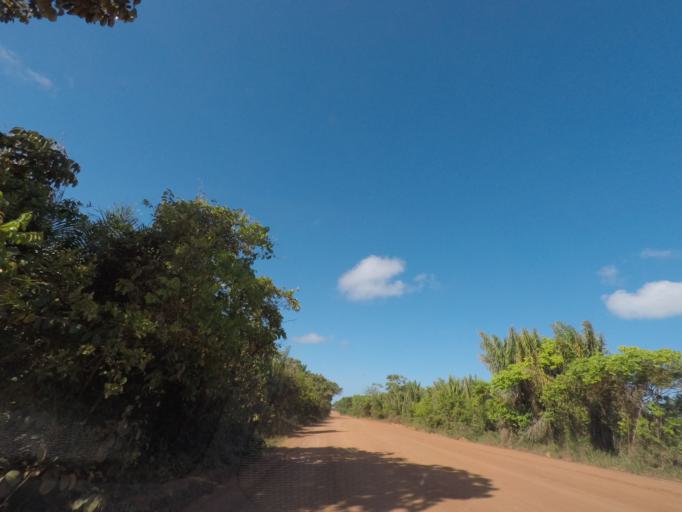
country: BR
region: Bahia
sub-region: Marau
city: Marau
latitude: -14.1407
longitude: -39.0006
